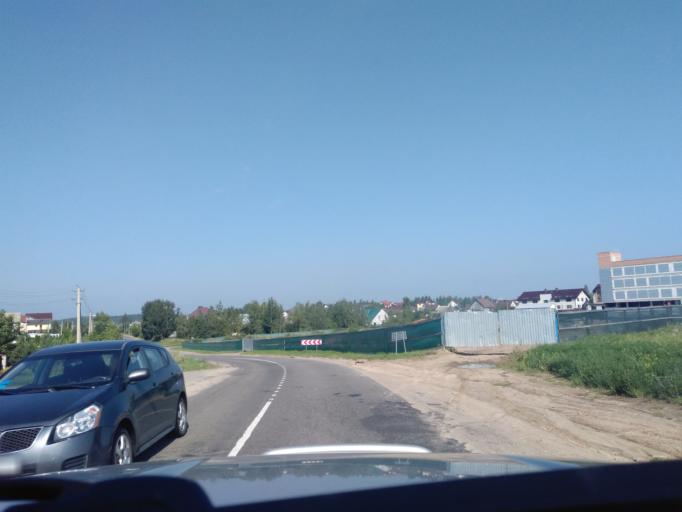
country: BY
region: Minsk
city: Zhdanovichy
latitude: 53.9320
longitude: 27.4159
